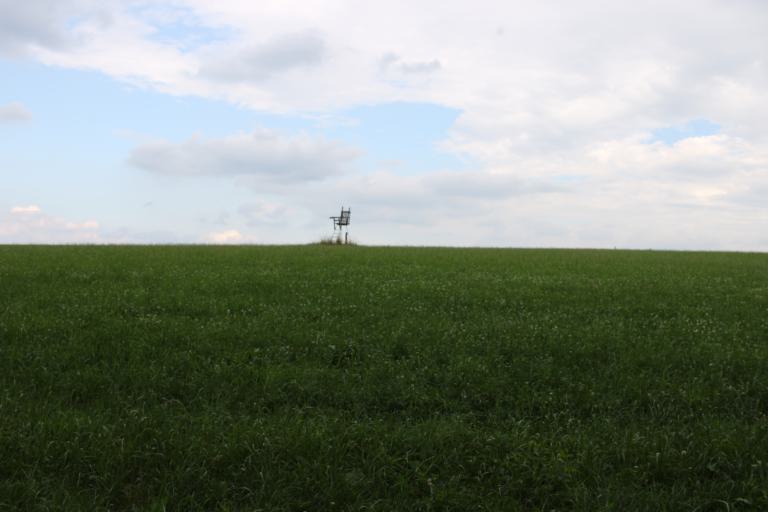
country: DE
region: Hesse
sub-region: Regierungsbezirk Darmstadt
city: Erbach
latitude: 49.6484
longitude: 8.9507
